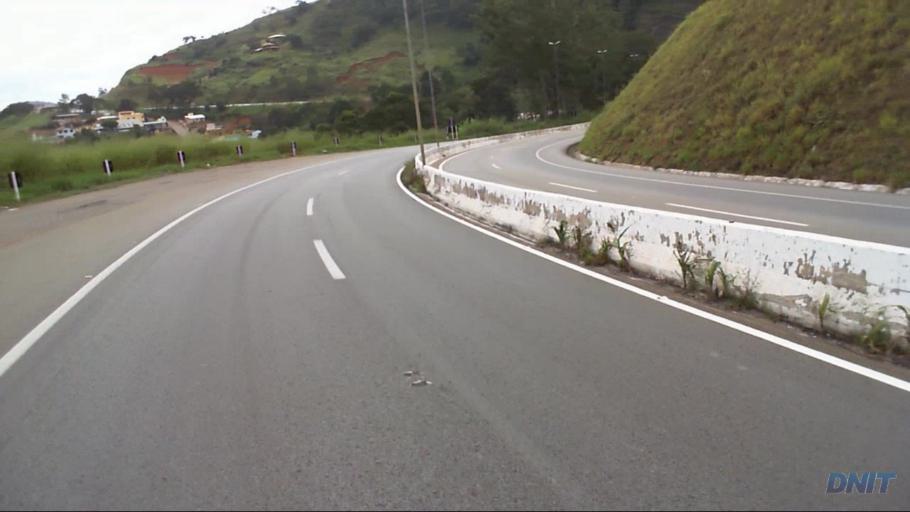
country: BR
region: Minas Gerais
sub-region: Nova Era
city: Nova Era
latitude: -19.7613
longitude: -43.0316
